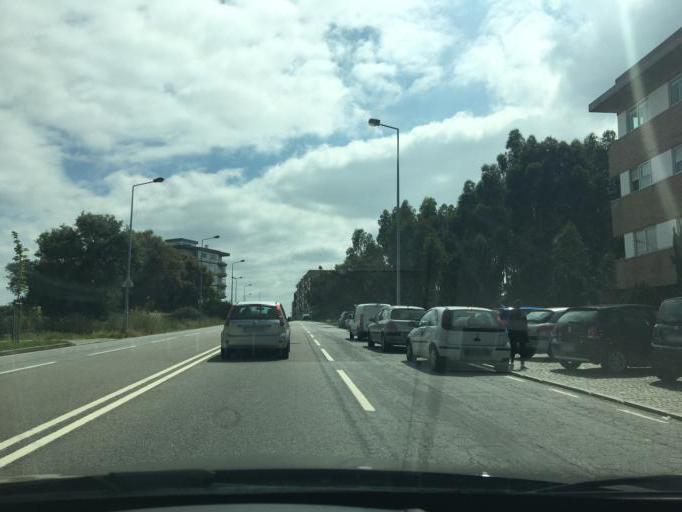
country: PT
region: Porto
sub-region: Maia
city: Anta
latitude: 41.2596
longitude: -8.6197
